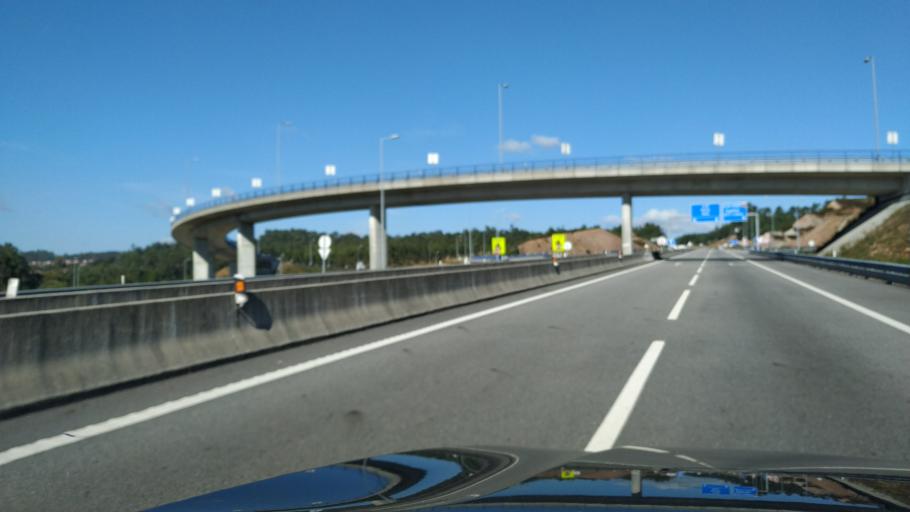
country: PT
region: Porto
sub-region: Vila Nova de Gaia
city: Sandim
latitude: 41.0369
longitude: -8.4930
